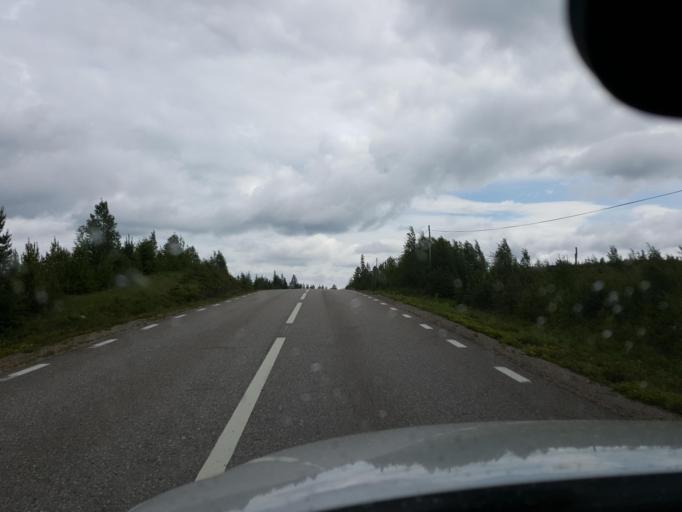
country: SE
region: Gaevleborg
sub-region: Ljusdals Kommun
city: Farila
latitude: 61.7608
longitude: 15.5093
